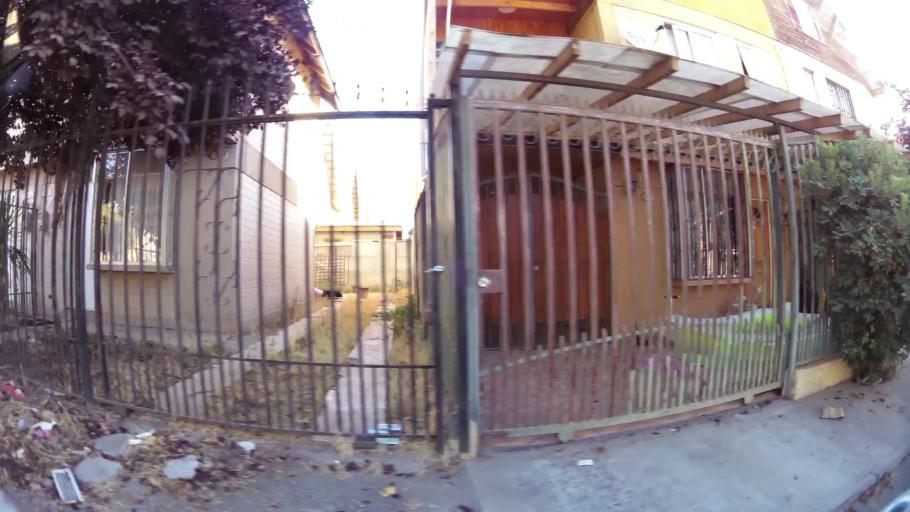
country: CL
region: O'Higgins
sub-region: Provincia de Cachapoal
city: Rancagua
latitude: -34.1828
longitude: -70.7628
